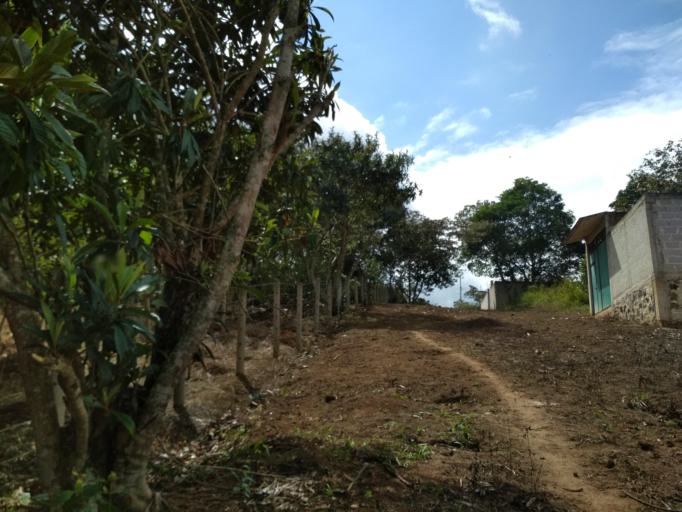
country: MX
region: Veracruz
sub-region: Emiliano Zapata
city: Jacarandas
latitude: 19.4976
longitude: -96.8348
